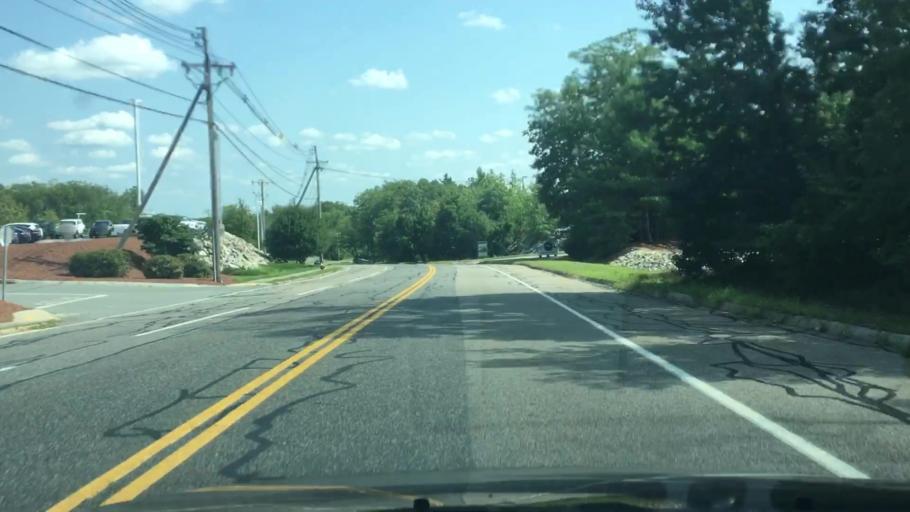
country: US
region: Massachusetts
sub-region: Worcester County
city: Milford
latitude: 42.1591
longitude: -71.4960
